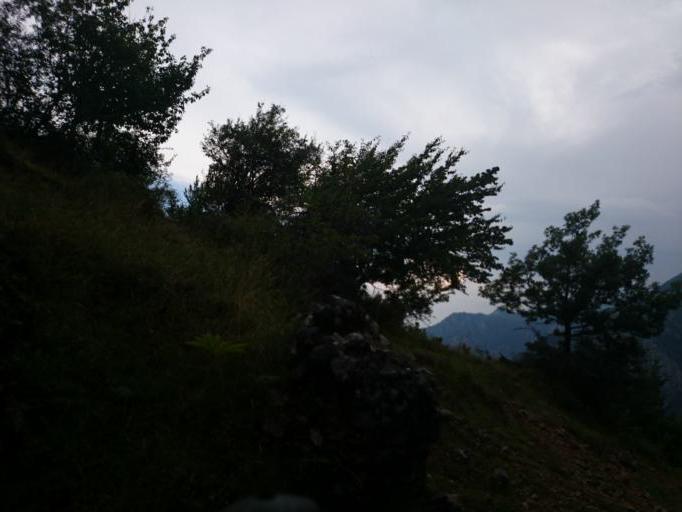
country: AL
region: Diber
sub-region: Rrethi i Dibres
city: Fushe-Lure
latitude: 41.7683
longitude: 20.2272
